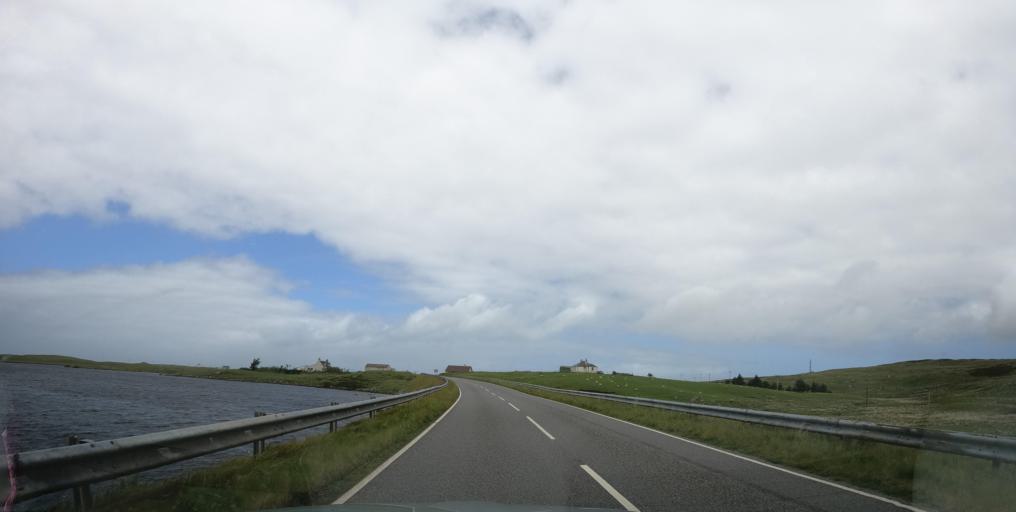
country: GB
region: Scotland
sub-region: Eilean Siar
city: Isle of South Uist
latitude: 57.2976
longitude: -7.3658
